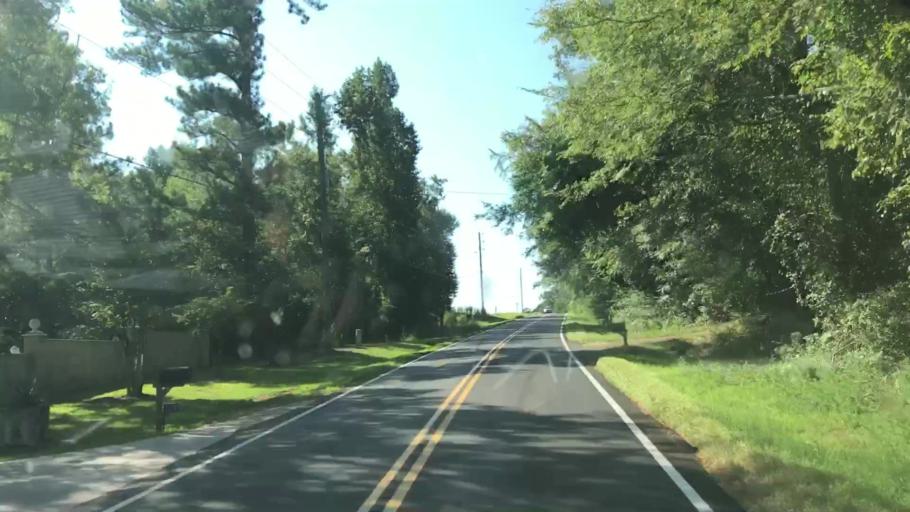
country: US
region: Georgia
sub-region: Walton County
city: Monroe
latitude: 33.8518
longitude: -83.7865
